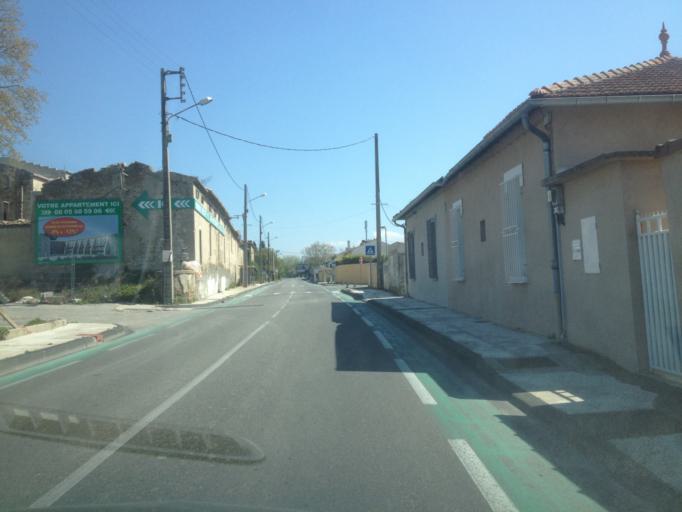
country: FR
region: Provence-Alpes-Cote d'Azur
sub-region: Departement du Vaucluse
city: Le Pontet
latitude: 43.9628
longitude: 4.8679
